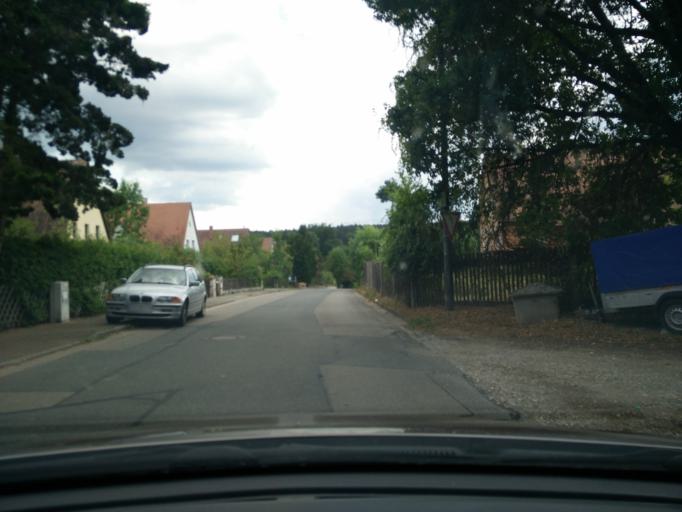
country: DE
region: Bavaria
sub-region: Regierungsbezirk Mittelfranken
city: Oberasbach
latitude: 49.3723
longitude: 10.9802
